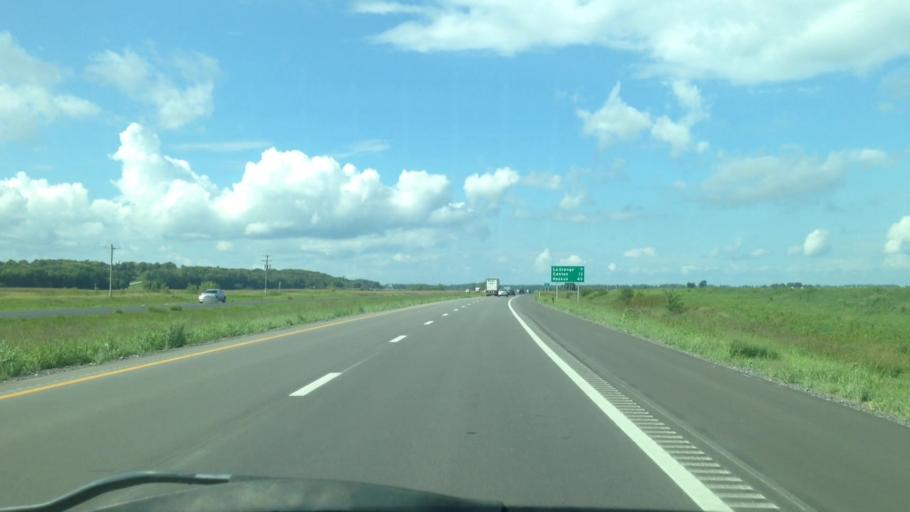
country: US
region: Illinois
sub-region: Adams County
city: Quincy
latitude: 39.9438
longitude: -91.5185
